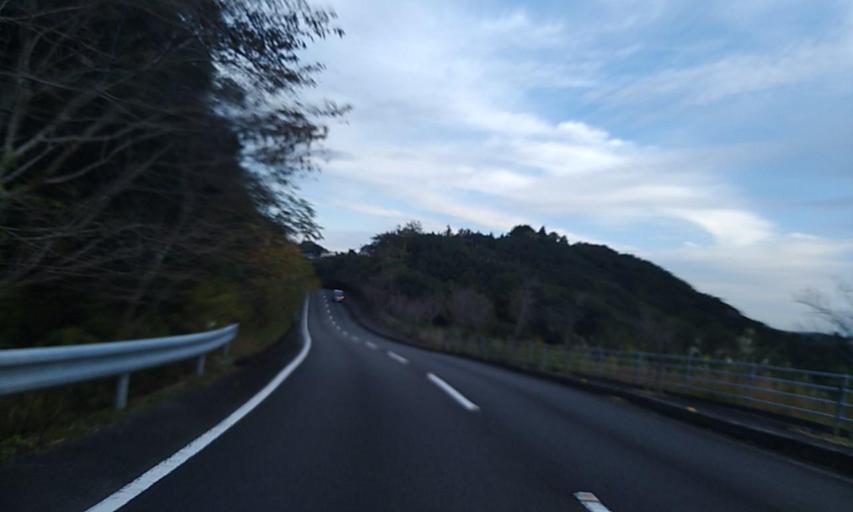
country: JP
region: Mie
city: Toba
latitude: 34.3340
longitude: 136.8080
